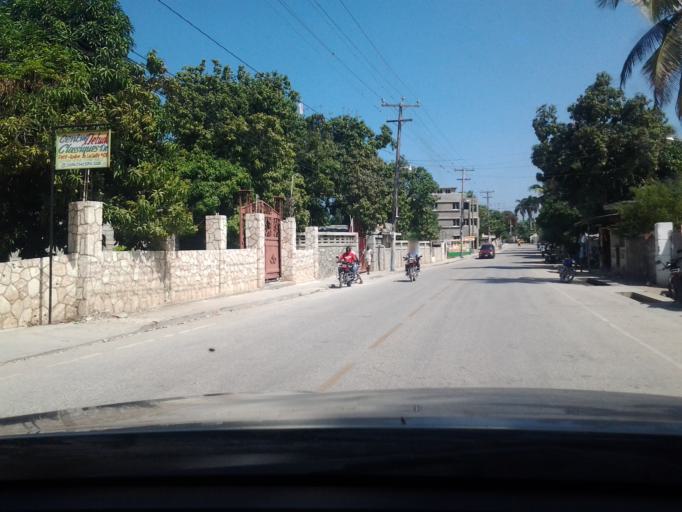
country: HT
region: Ouest
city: Tigwav
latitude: 18.4385
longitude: -72.8538
